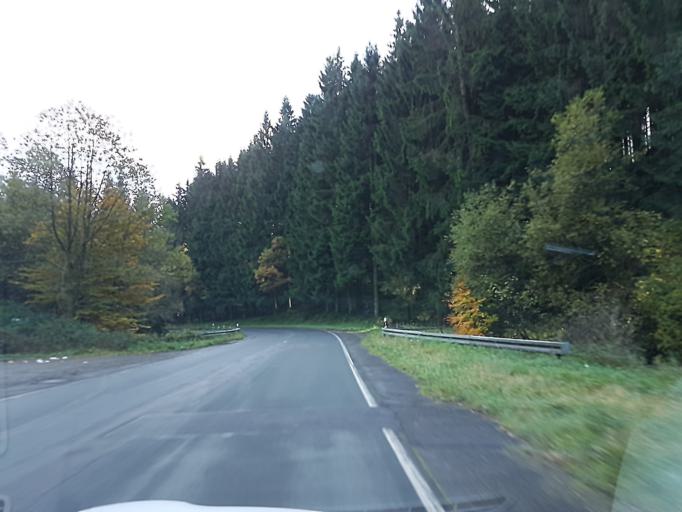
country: DE
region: North Rhine-Westphalia
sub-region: Regierungsbezirk Arnsberg
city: Drolshagen
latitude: 51.0874
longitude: 7.7908
